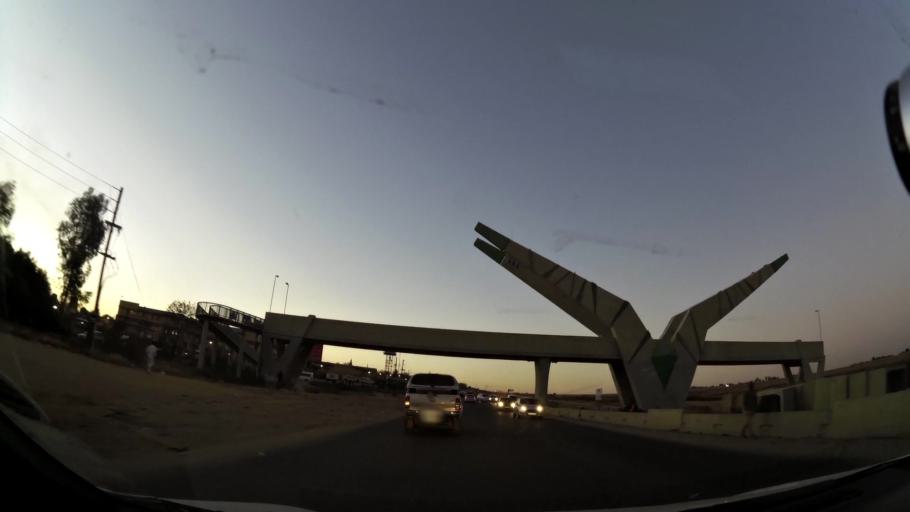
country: ZA
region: Gauteng
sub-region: City of Johannesburg Metropolitan Municipality
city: Diepsloot
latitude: -25.9238
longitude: 28.0227
